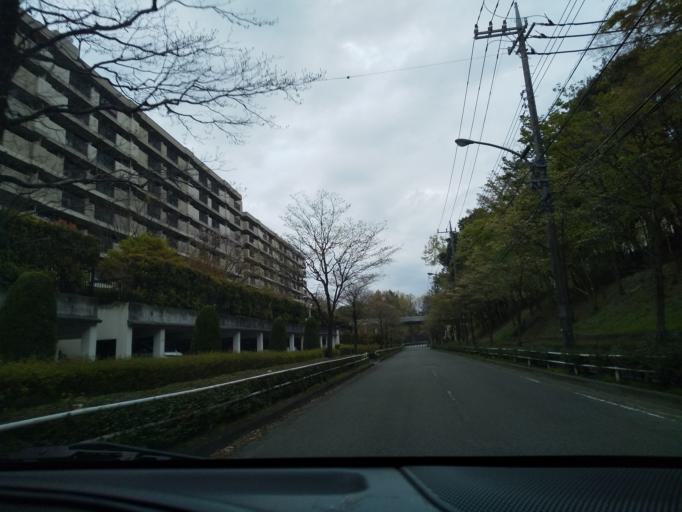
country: JP
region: Tokyo
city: Hino
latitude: 35.6094
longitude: 139.3803
